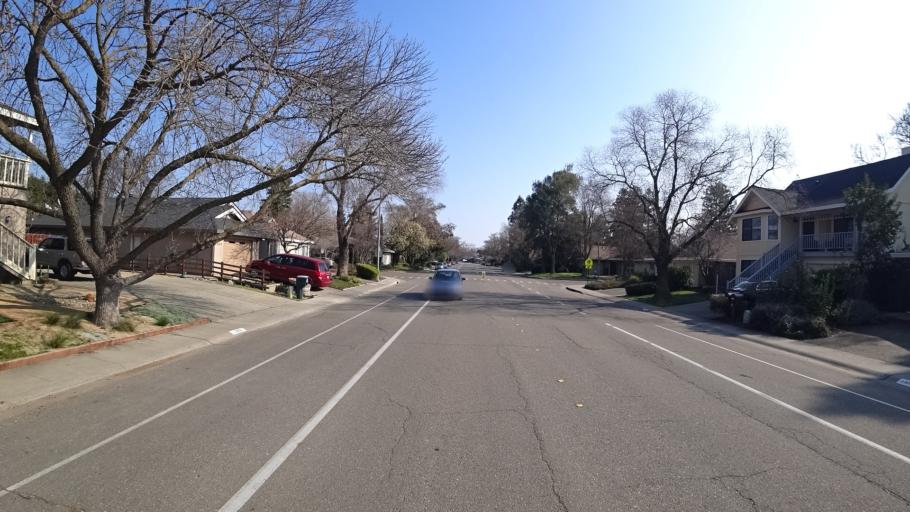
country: US
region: California
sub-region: Yolo County
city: Davis
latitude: 38.5528
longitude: -121.7744
